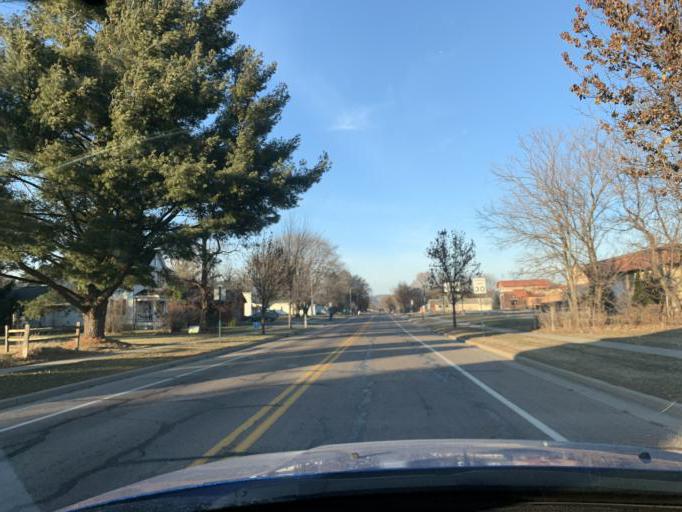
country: US
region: Wisconsin
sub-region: Sauk County
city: Spring Green
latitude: 43.1723
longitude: -90.0640
